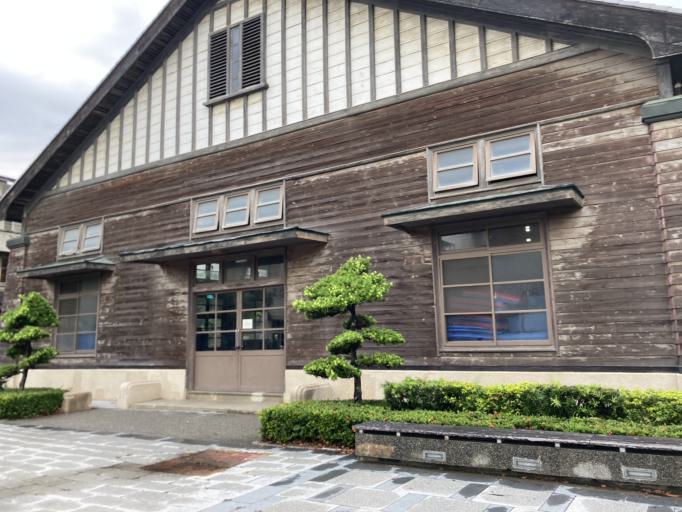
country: TW
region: Taiwan
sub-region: Yunlin
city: Douliu
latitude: 23.9004
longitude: 120.3710
